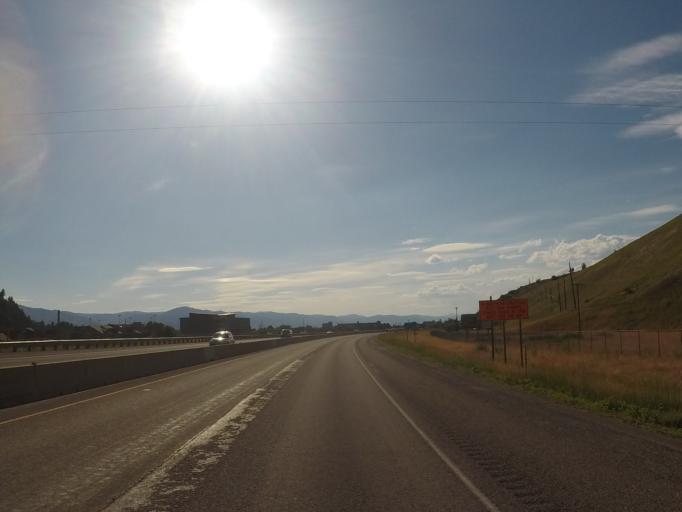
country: US
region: Montana
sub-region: Missoula County
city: East Missoula
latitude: 46.8641
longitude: -113.9683
